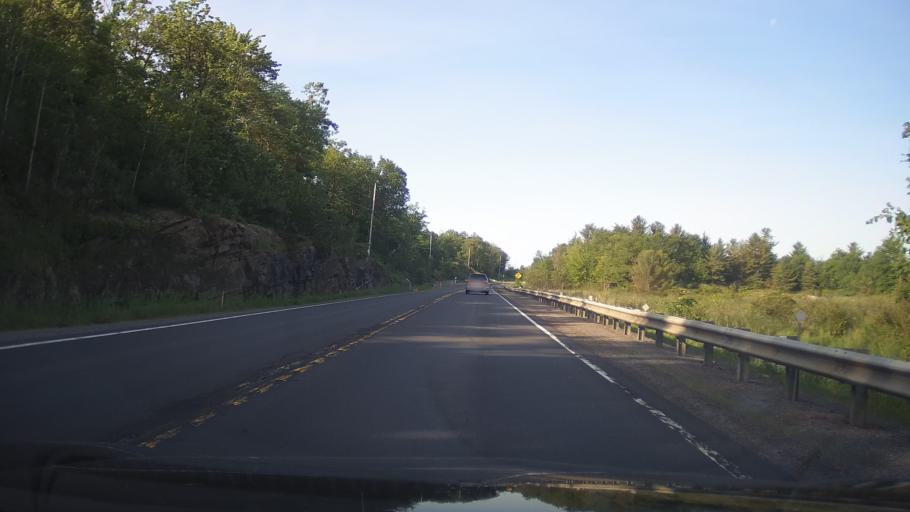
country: CA
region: Ontario
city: Greater Napanee
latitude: 44.6014
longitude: -77.1861
